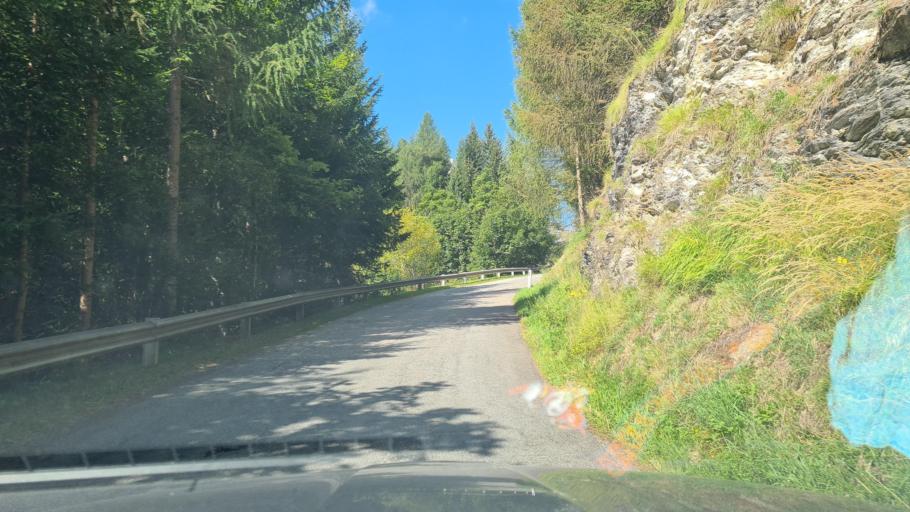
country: AT
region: Salzburg
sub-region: Politischer Bezirk Tamsweg
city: Zederhaus
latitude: 47.1836
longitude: 13.4385
